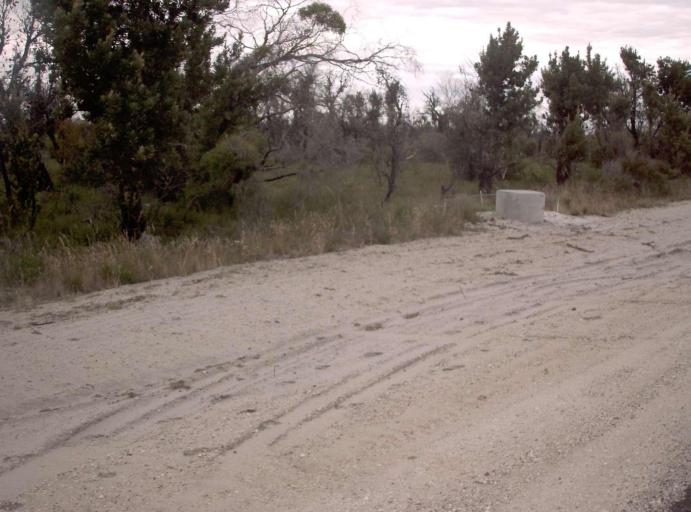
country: AU
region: Victoria
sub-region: East Gippsland
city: Bairnsdale
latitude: -38.1239
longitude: 147.4508
